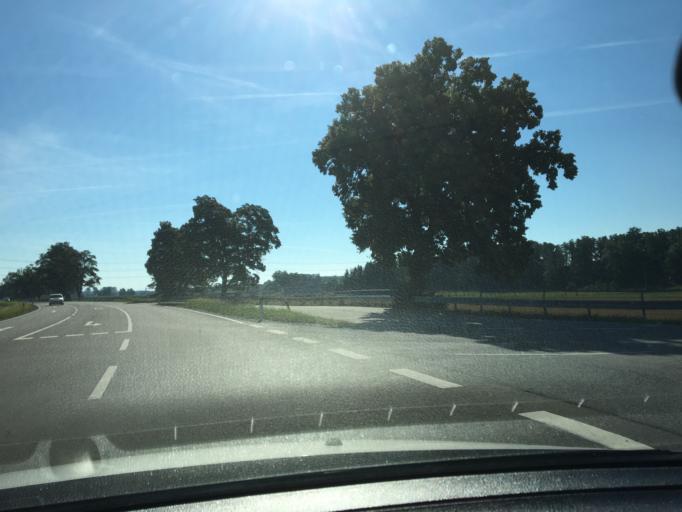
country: DE
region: Bavaria
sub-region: Upper Bavaria
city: Taufkirchen
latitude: 48.3463
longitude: 12.1433
